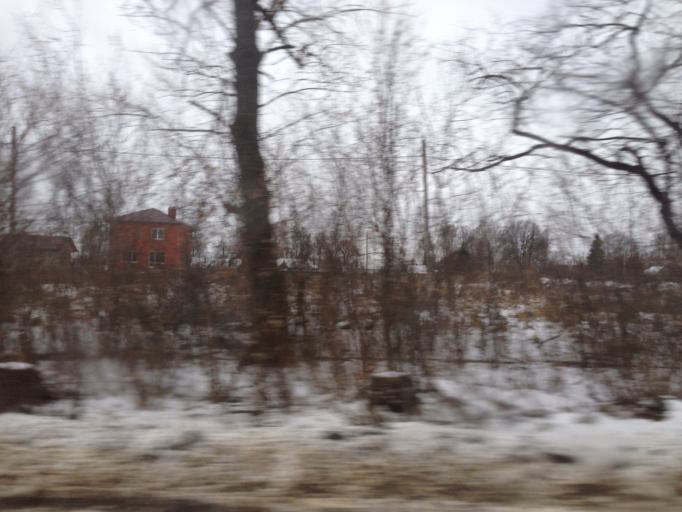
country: RU
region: Tula
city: Uzlovaya
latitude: 53.9943
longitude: 38.1375
